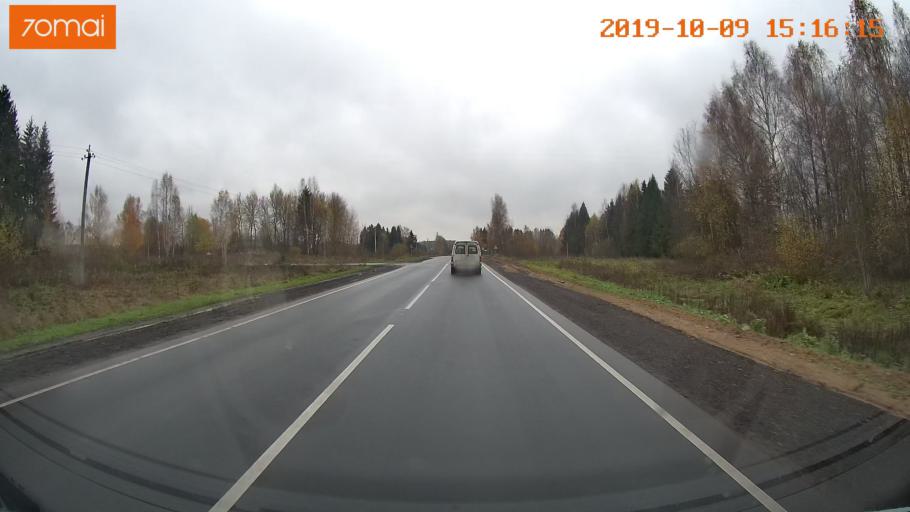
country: RU
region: Kostroma
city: Susanino
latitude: 58.1119
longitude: 41.5864
